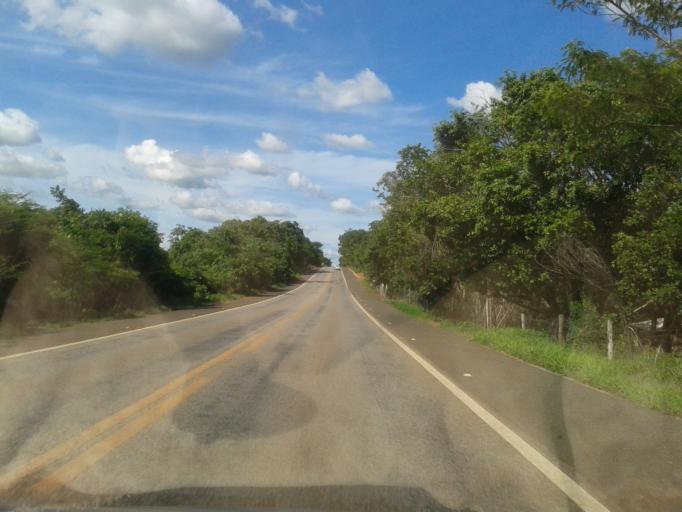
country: BR
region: Goias
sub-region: Mozarlandia
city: Mozarlandia
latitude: -15.0686
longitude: -50.6173
